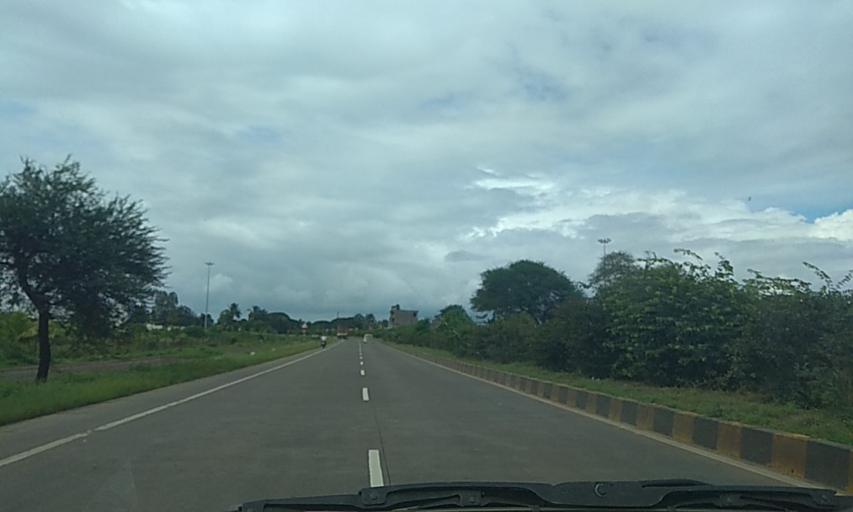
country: IN
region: Maharashtra
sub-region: Kolhapur
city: Kagal
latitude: 16.5635
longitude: 74.3165
